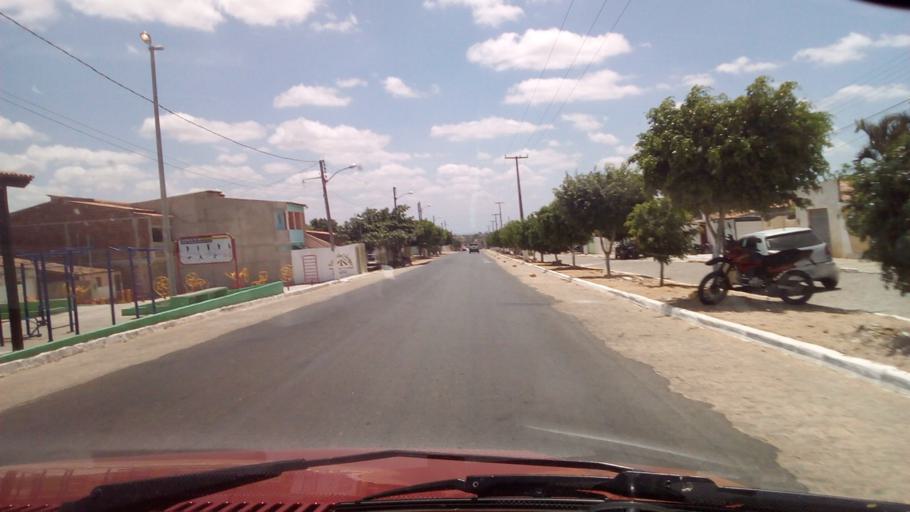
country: BR
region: Paraiba
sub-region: Cacimba De Dentro
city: Cacimba de Dentro
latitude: -6.6316
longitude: -35.7980
